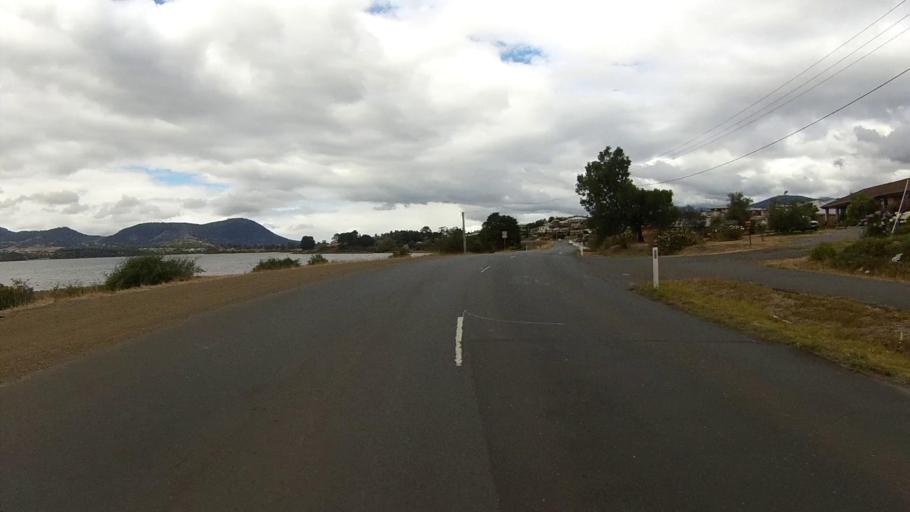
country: AU
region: Tasmania
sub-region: Glenorchy
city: Granton
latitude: -42.7561
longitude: 147.2353
